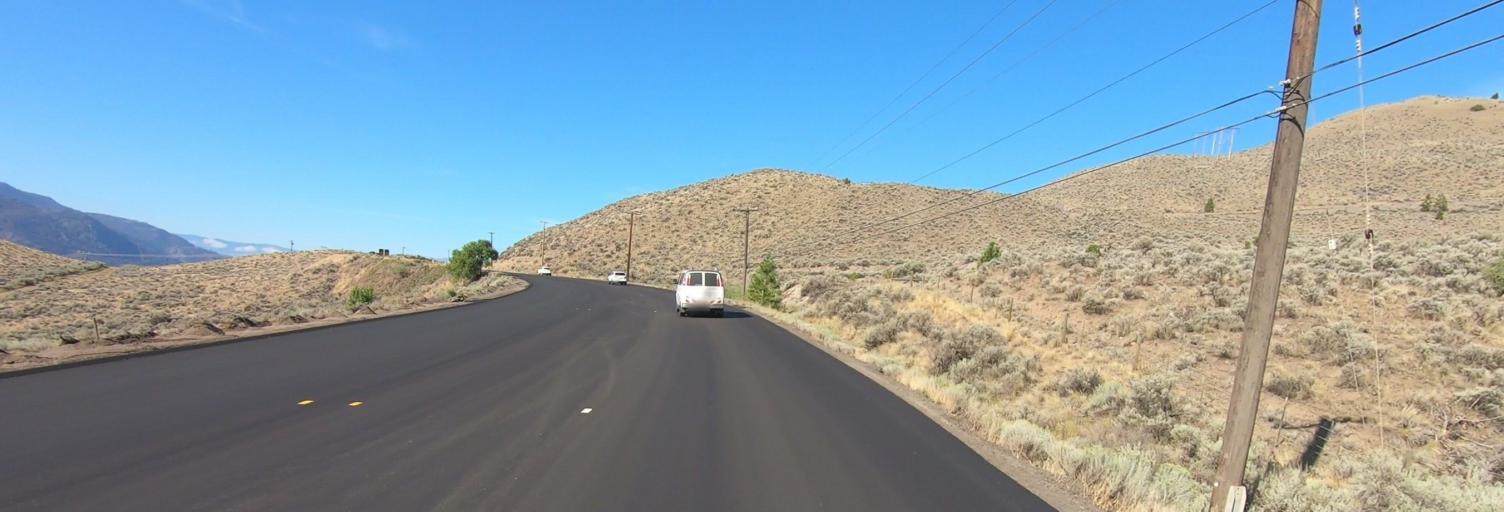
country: CA
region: British Columbia
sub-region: Thompson-Nicola Regional District
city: Ashcroft
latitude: 50.7986
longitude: -121.1062
